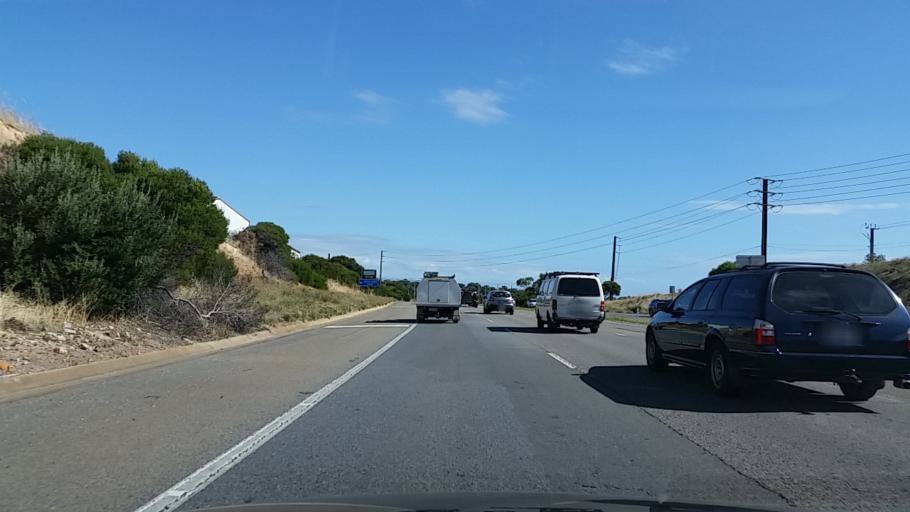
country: AU
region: South Australia
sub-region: Onkaparinga
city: Morphett Vale
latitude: -35.1142
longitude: 138.4916
